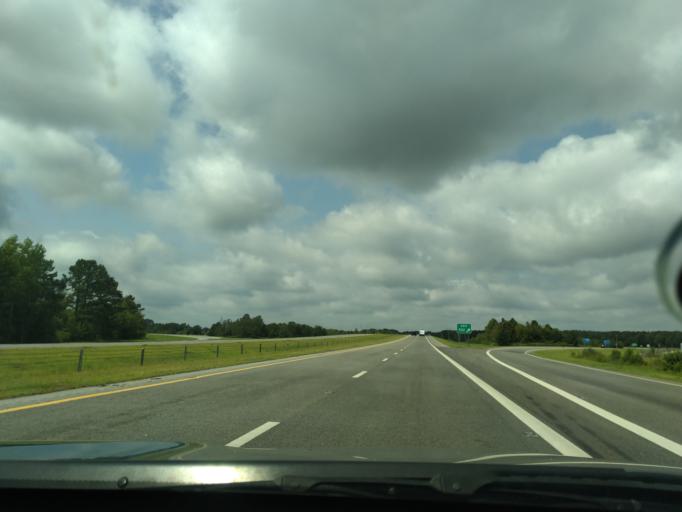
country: US
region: North Carolina
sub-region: Martin County
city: Robersonville
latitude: 35.8384
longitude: -77.2467
